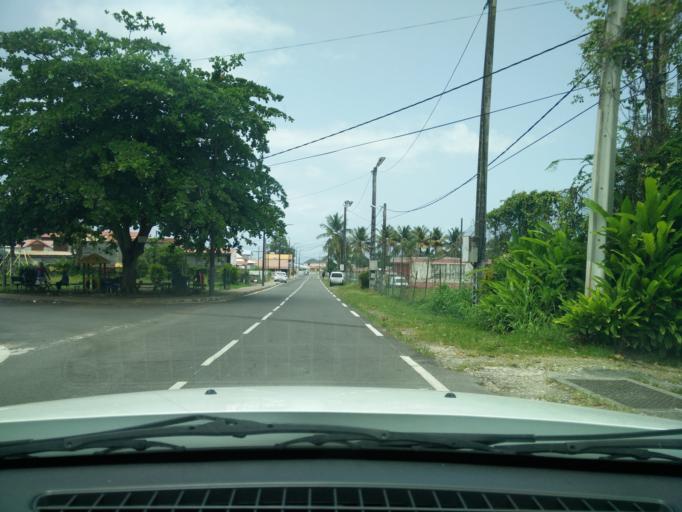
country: GP
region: Guadeloupe
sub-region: Guadeloupe
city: Capesterre-Belle-Eau
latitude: 16.0531
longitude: -61.5604
